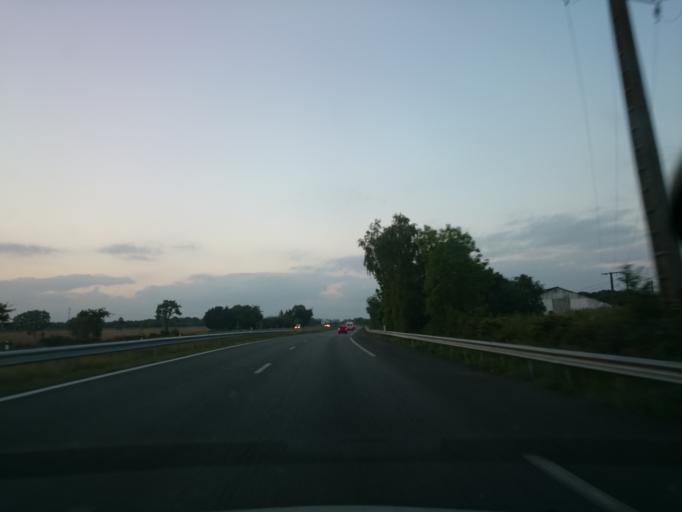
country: FR
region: Brittany
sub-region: Departement d'Ille-et-Vilaine
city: Pance
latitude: 47.9033
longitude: -1.6857
